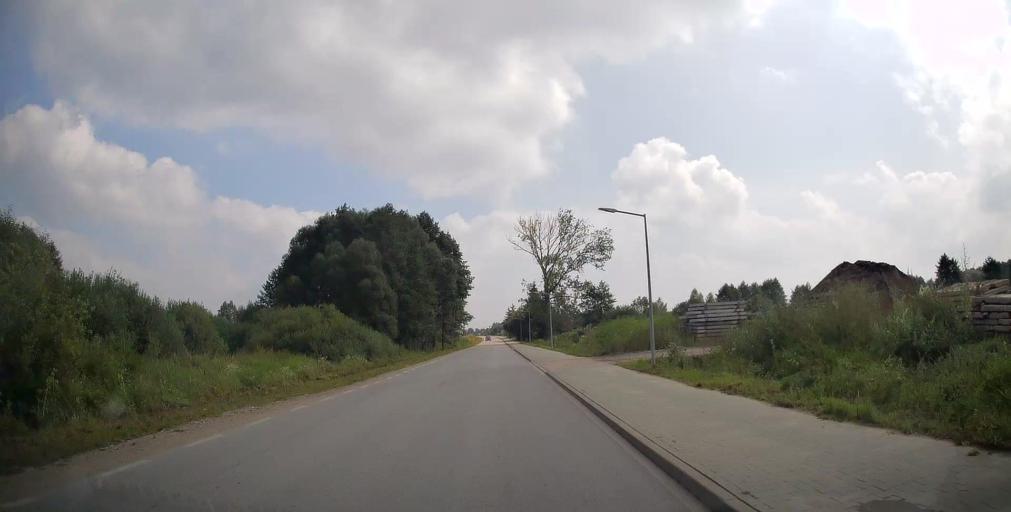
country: PL
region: Masovian Voivodeship
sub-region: Powiat bialobrzeski
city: Sucha
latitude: 51.6130
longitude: 20.9667
